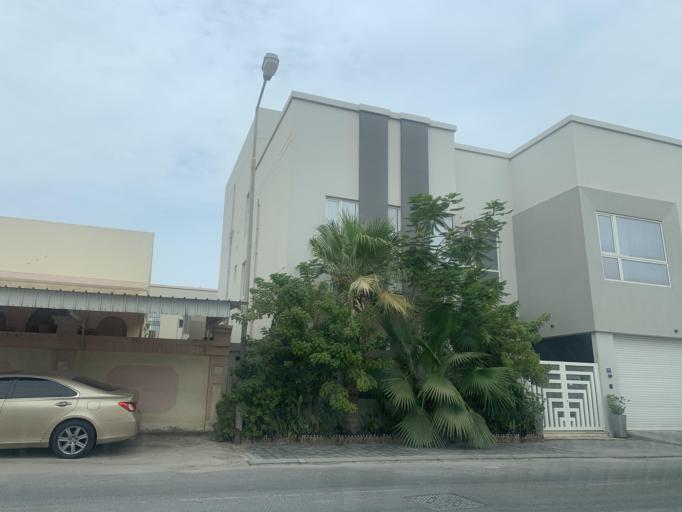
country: BH
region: Muharraq
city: Al Muharraq
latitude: 26.2793
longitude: 50.6385
